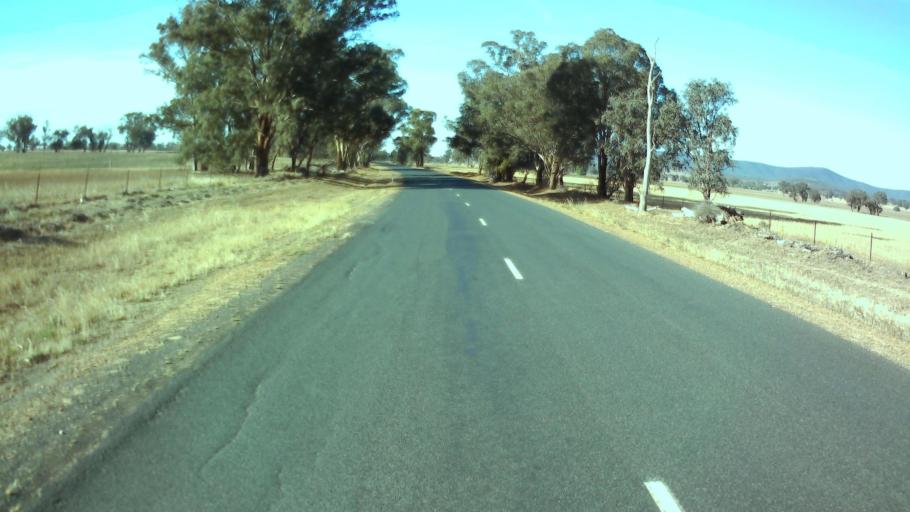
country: AU
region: New South Wales
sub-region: Weddin
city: Grenfell
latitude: -33.9242
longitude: 148.1388
